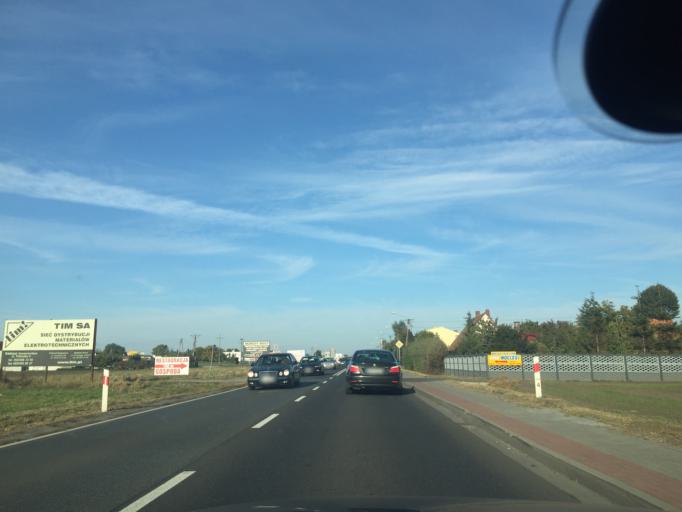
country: PL
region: Kujawsko-Pomorskie
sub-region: Powiat inowroclawski
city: Inowroclaw
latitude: 52.7406
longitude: 18.2485
